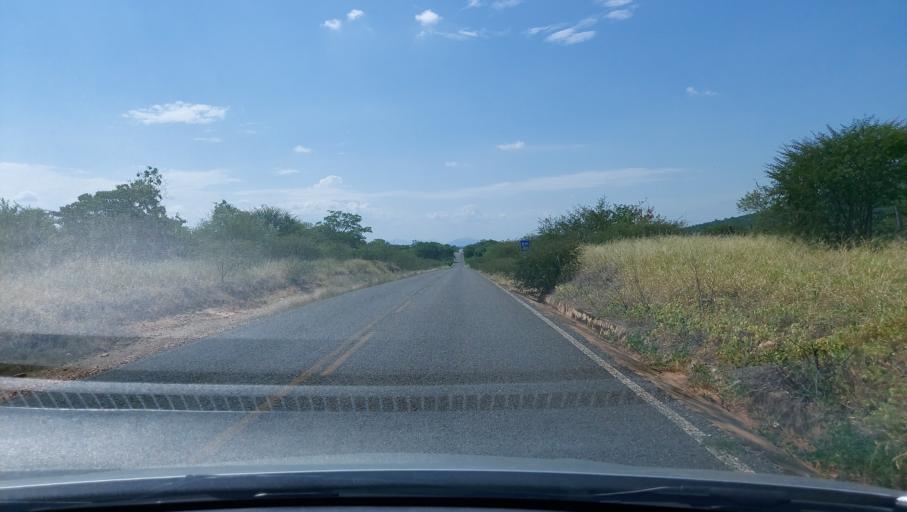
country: BR
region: Bahia
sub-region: Oliveira Dos Brejinhos
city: Beira Rio
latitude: -12.1653
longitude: -42.5480
